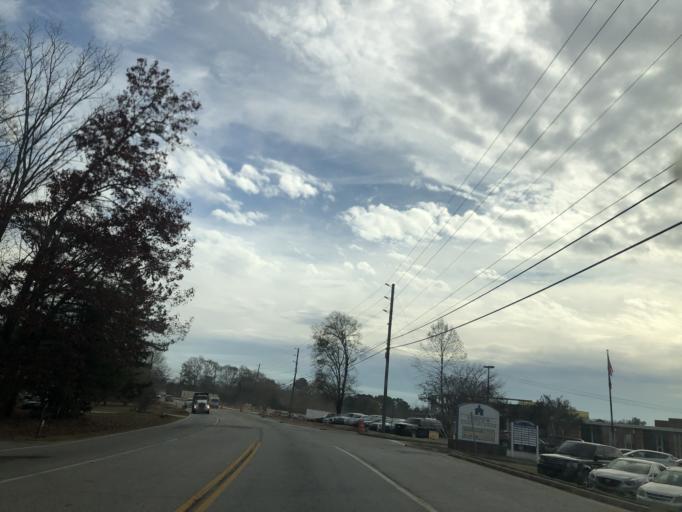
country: US
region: Georgia
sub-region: Henry County
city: Stockbridge
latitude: 33.6103
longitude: -84.2280
